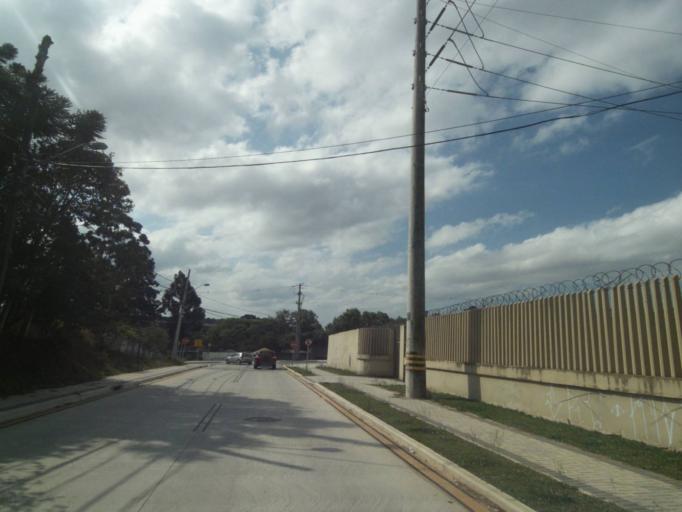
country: BR
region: Parana
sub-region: Pinhais
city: Pinhais
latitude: -25.4097
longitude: -49.2179
